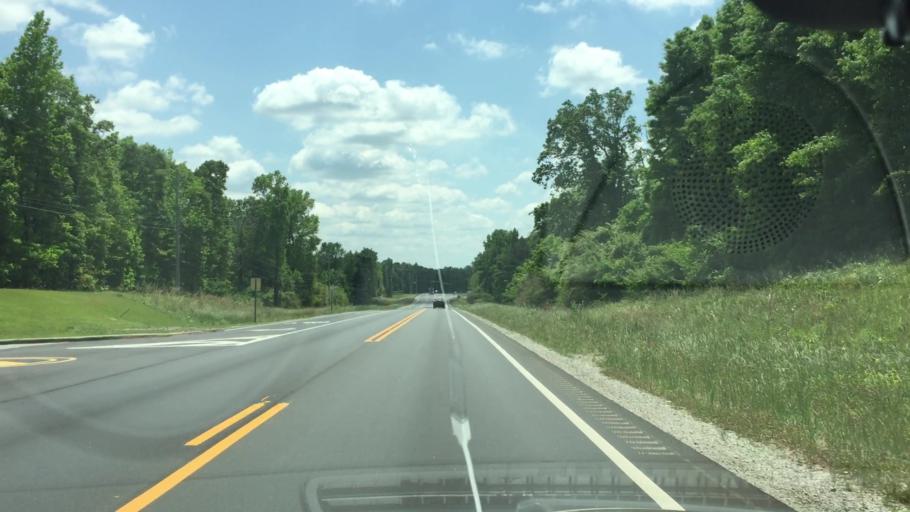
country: US
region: Alabama
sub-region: Lee County
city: Opelika
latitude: 32.6598
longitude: -85.3602
